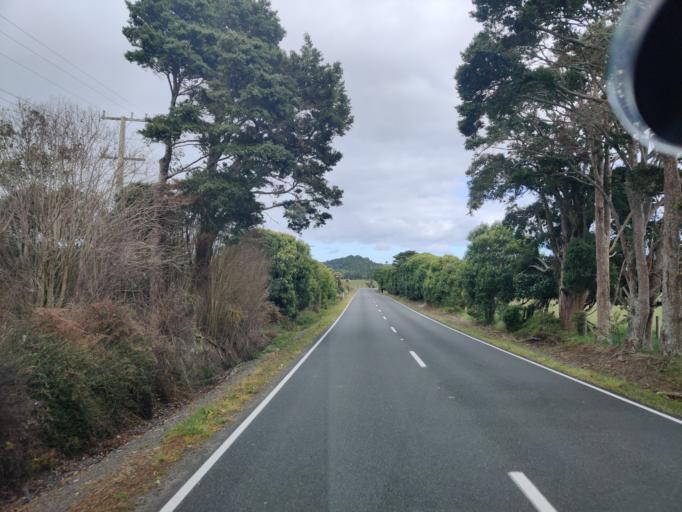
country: NZ
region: Northland
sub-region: Whangarei
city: Ngunguru
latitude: -35.5667
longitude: 174.3951
